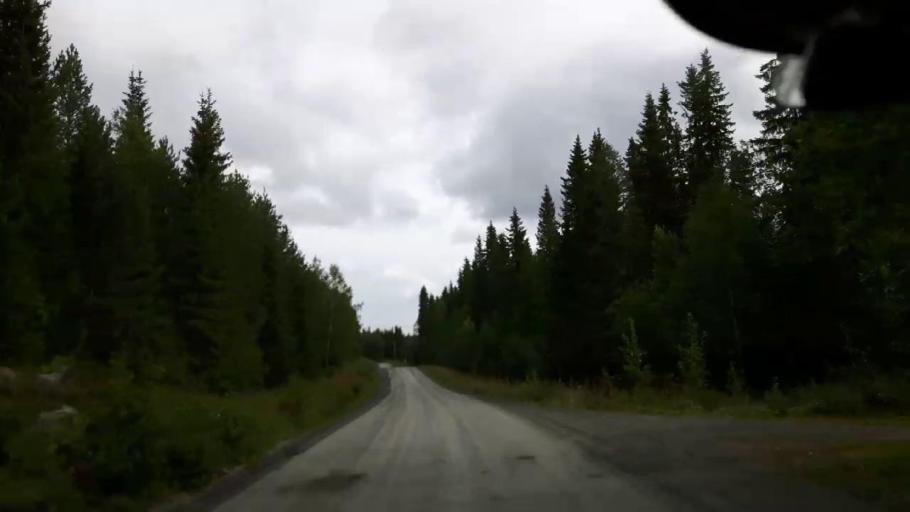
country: SE
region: Jaemtland
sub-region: Krokoms Kommun
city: Valla
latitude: 63.6150
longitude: 14.0908
